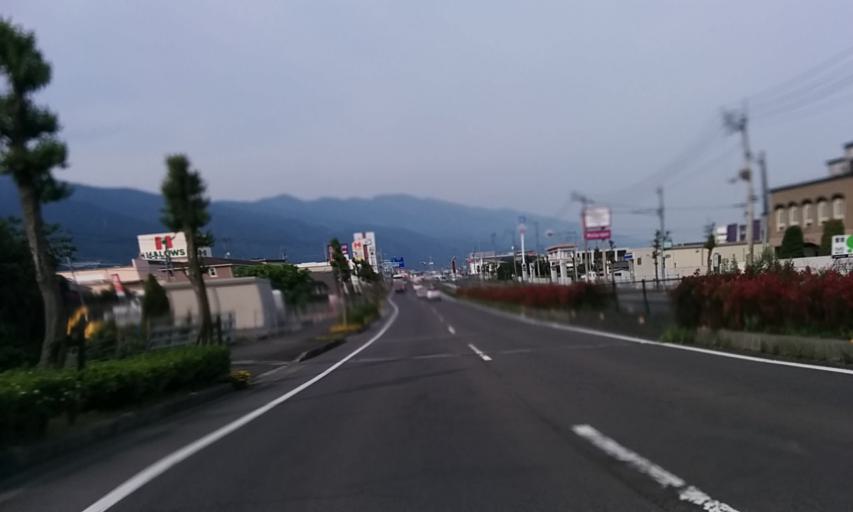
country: JP
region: Ehime
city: Kawanoecho
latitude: 33.9819
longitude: 133.5556
